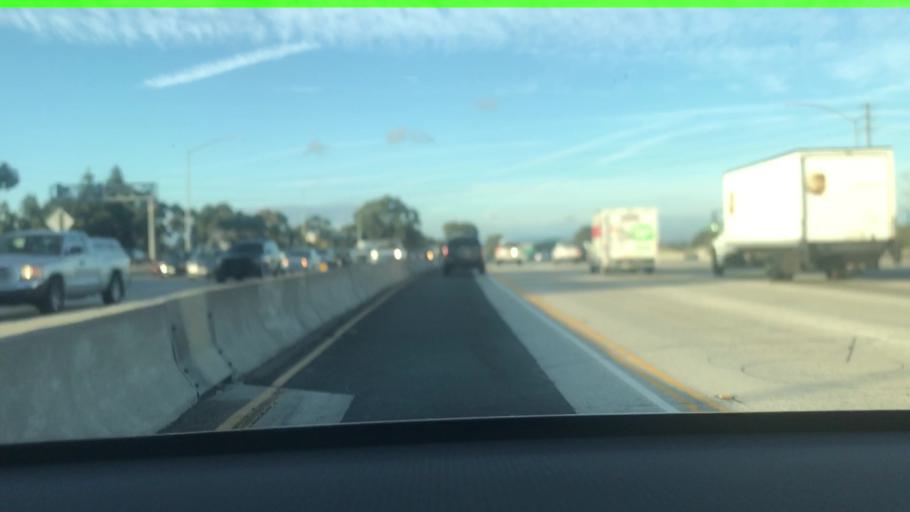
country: US
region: California
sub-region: Los Angeles County
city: Del Aire
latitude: 33.9150
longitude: -118.3704
